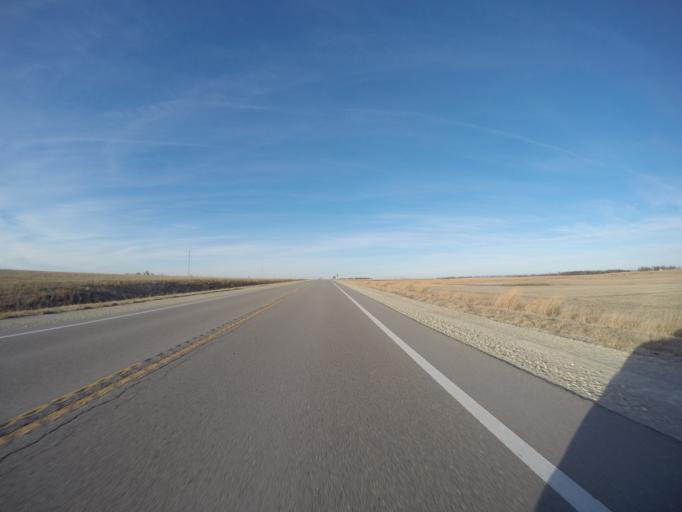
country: US
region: Kansas
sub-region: Marion County
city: Marion
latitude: 38.3562
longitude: -96.9667
